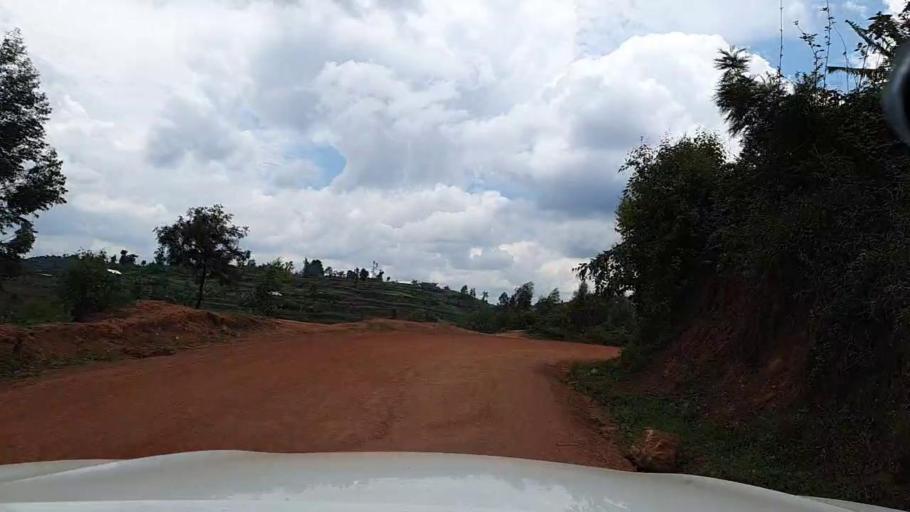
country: RW
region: Southern Province
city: Butare
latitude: -2.7080
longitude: 29.5477
